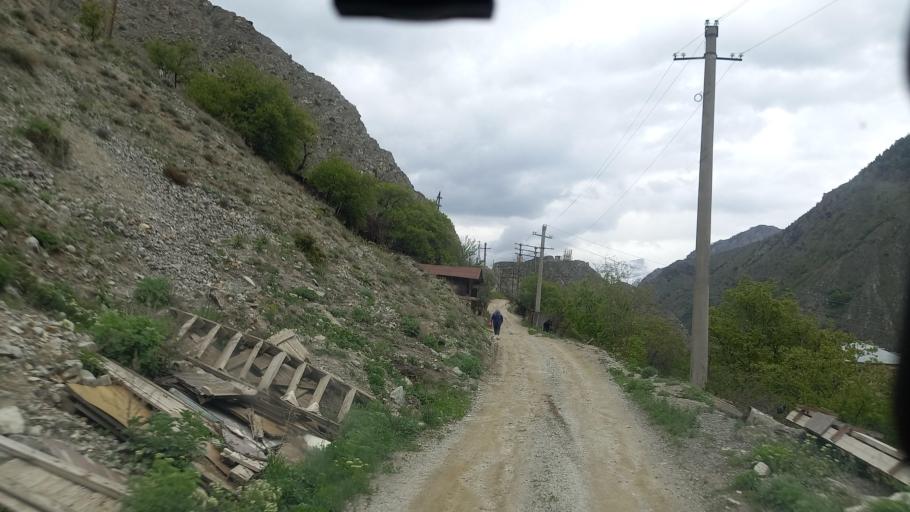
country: RU
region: North Ossetia
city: Mizur
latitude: 42.8527
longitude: 44.0700
